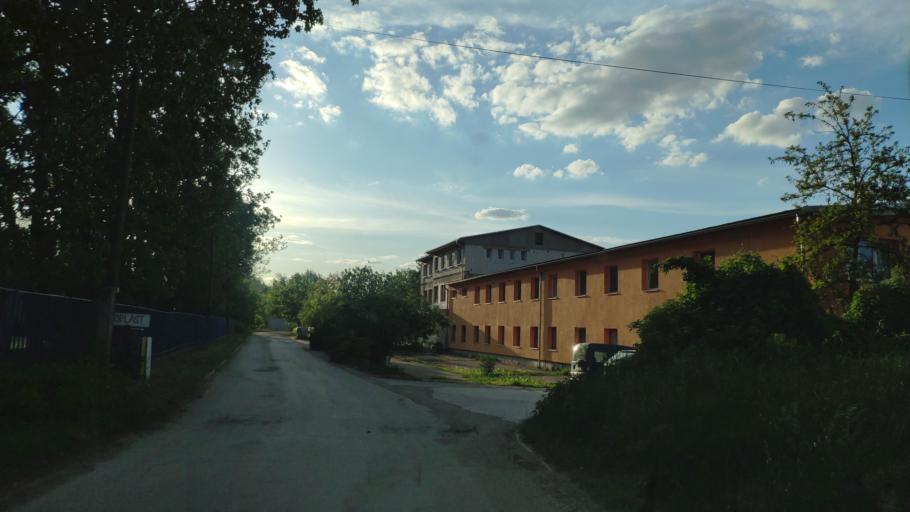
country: SK
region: Kosicky
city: Kosice
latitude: 48.6583
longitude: 21.3152
